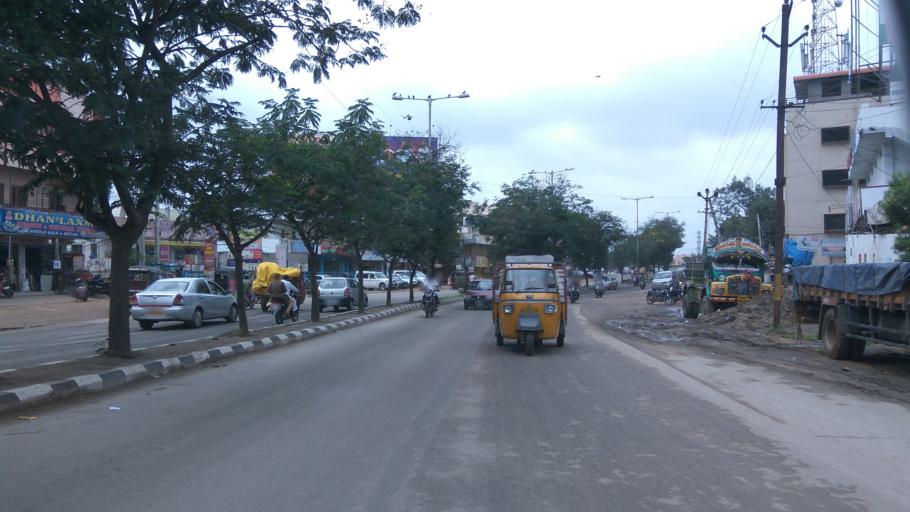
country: IN
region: Telangana
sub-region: Rangareddi
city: Secunderabad
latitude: 17.4829
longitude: 78.5393
